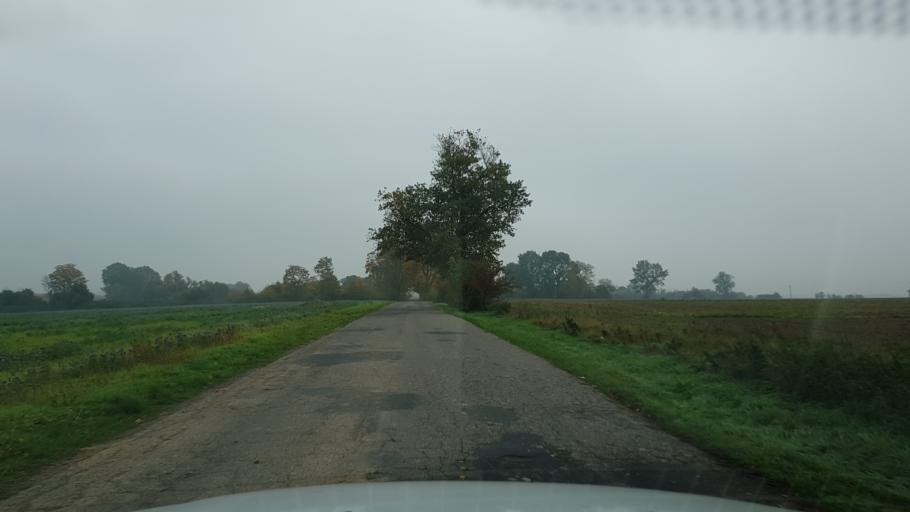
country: PL
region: West Pomeranian Voivodeship
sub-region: Powiat pyrzycki
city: Warnice
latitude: 53.2647
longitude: 15.0502
